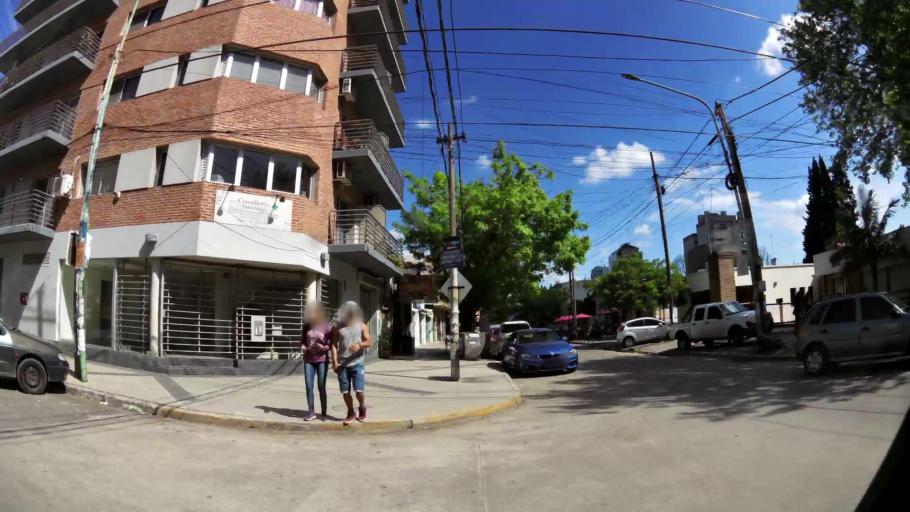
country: AR
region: Buenos Aires
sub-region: Partido de Quilmes
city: Quilmes
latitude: -34.8069
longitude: -58.2763
